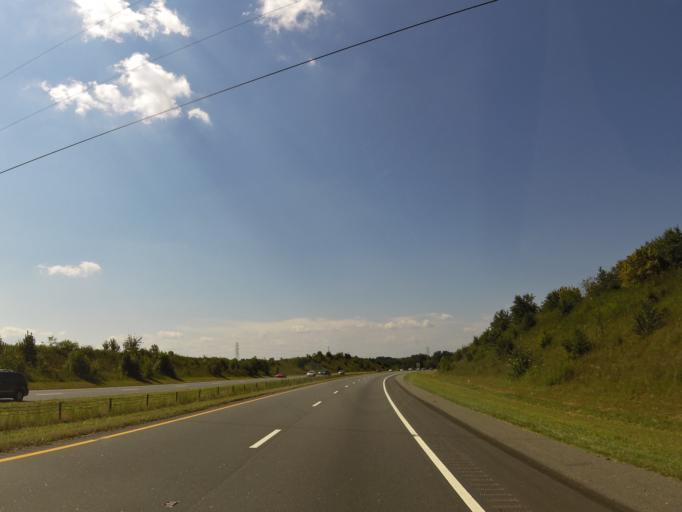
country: US
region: North Carolina
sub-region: Catawba County
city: Maiden
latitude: 35.5957
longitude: -81.2649
